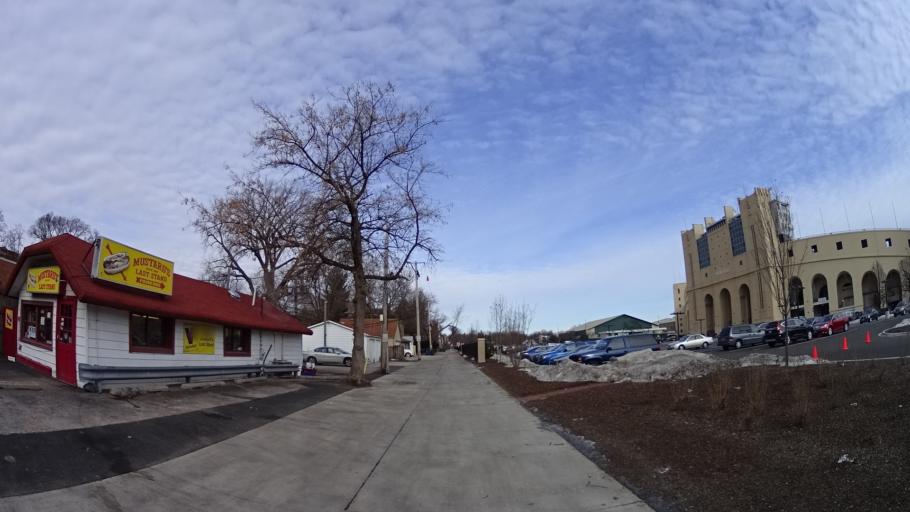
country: US
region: Illinois
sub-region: Cook County
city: Evanston
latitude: 42.0644
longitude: -87.6947
